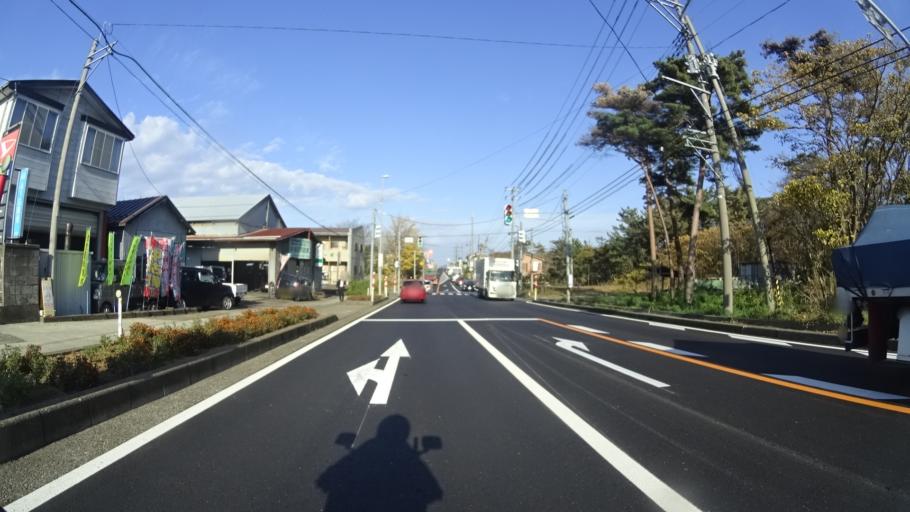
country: JP
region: Niigata
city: Joetsu
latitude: 37.2366
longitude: 138.3408
